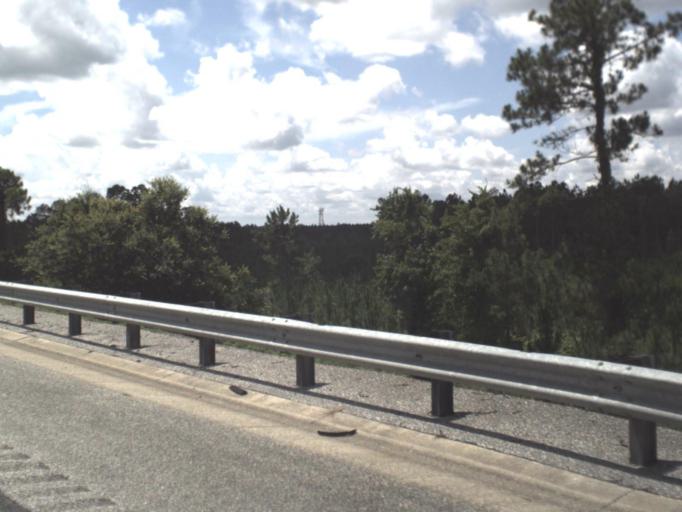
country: US
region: Florida
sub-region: Saint Johns County
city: Butler Beach
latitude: 29.6728
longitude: -81.3062
